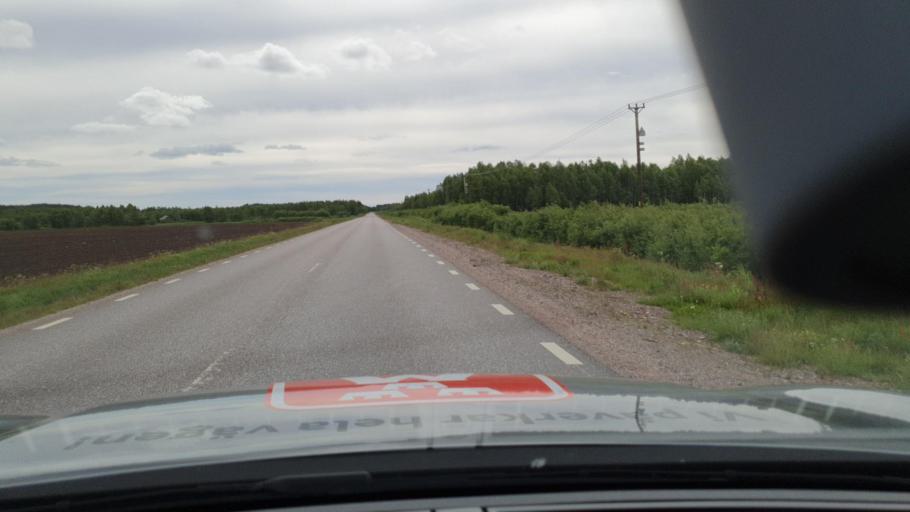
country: SE
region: Norrbotten
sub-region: Kalix Kommun
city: Kalix
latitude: 65.8900
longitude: 23.4692
